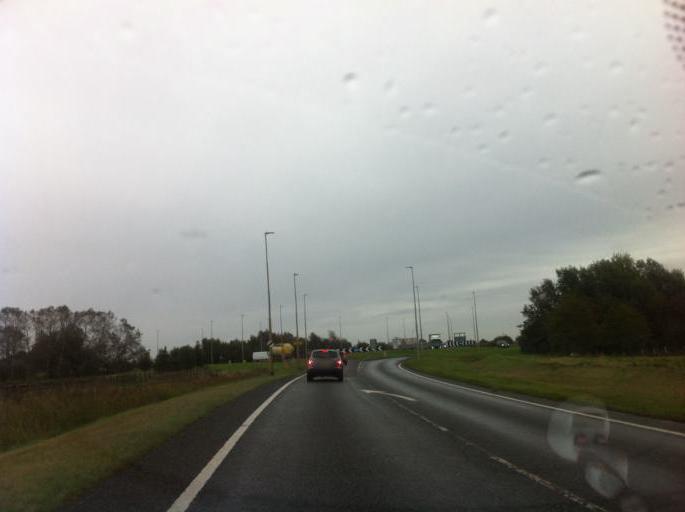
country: GB
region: England
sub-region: Lincolnshire
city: Crowland
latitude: 52.6628
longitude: -0.1735
